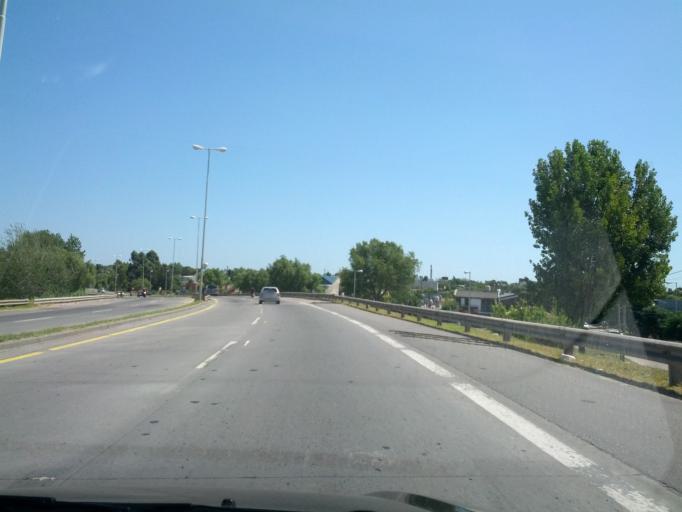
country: AR
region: Buenos Aires
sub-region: Partido de Campana
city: Campana
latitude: -34.1712
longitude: -58.9715
